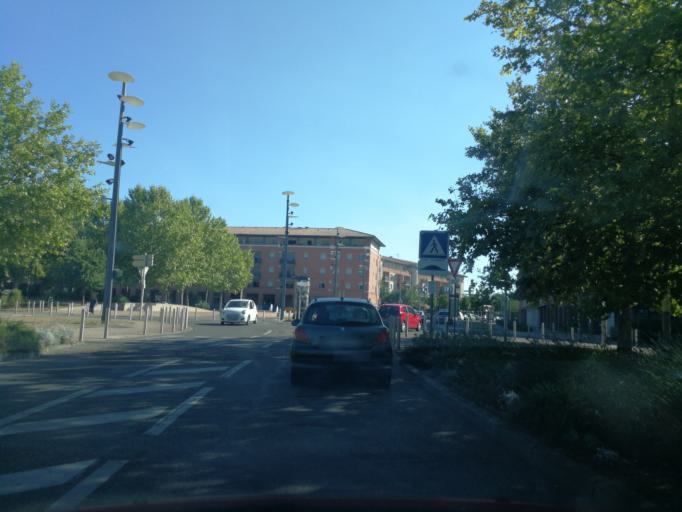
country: FR
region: Midi-Pyrenees
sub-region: Departement de la Haute-Garonne
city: Toulouse
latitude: 43.6296
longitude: 1.4494
